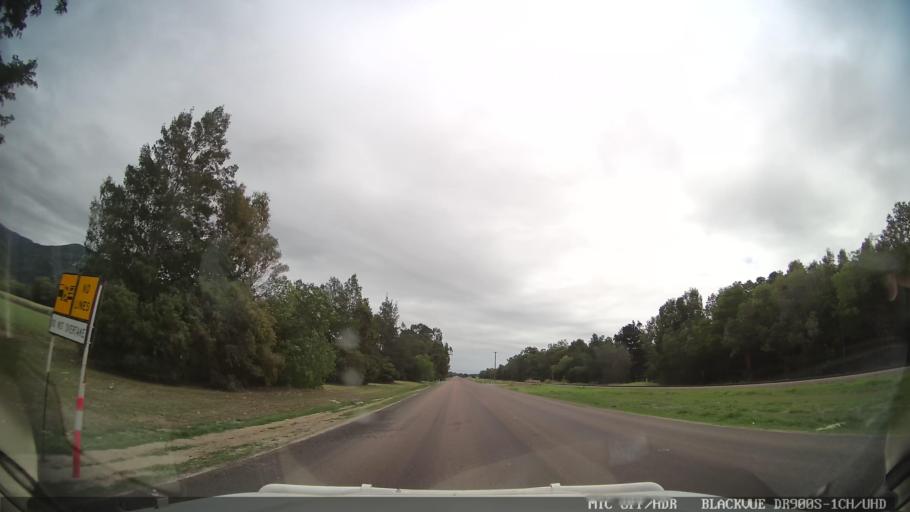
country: AU
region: Queensland
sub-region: Hinchinbrook
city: Ingham
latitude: -18.9305
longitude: 146.2666
